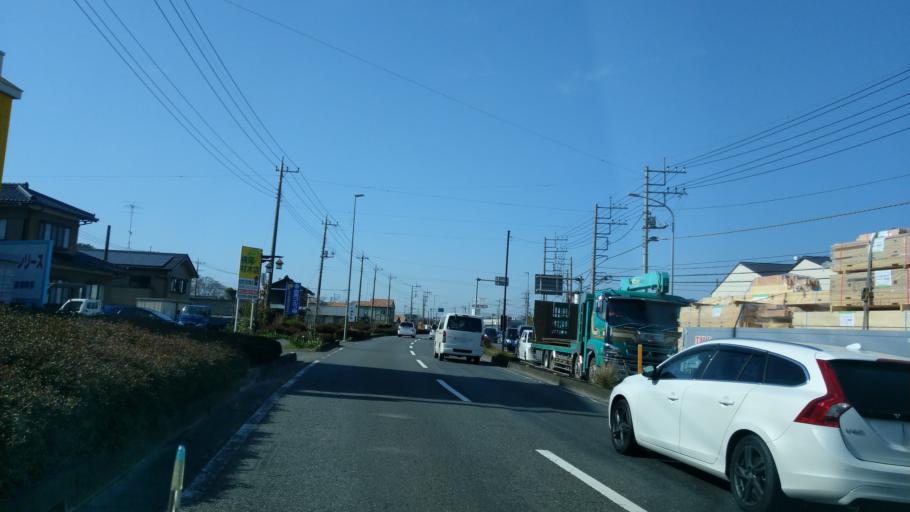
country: JP
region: Saitama
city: Sakado
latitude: 36.0113
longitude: 139.4359
